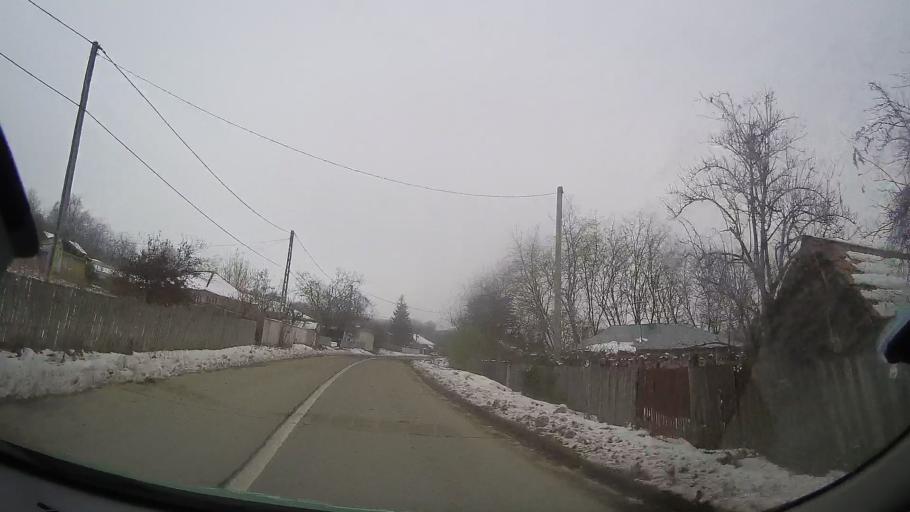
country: RO
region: Vrancea
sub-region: Comuna Boghesti
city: Boghesti
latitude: 46.2004
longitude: 27.4428
